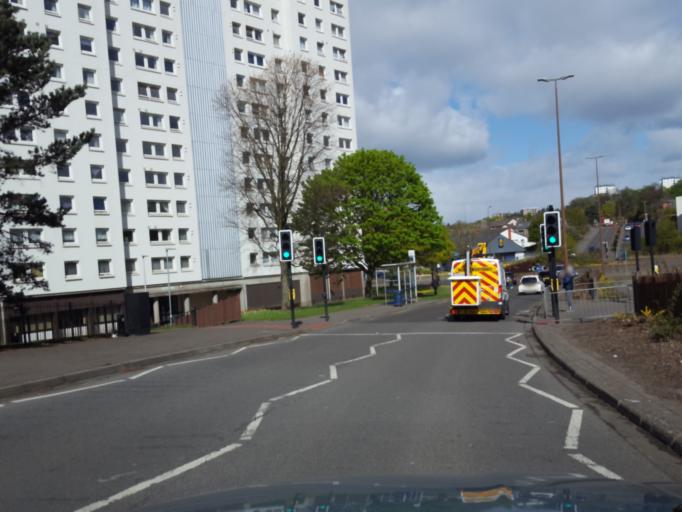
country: GB
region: Scotland
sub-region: Dundee City
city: Dundee
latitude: 56.4712
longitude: -3.0114
